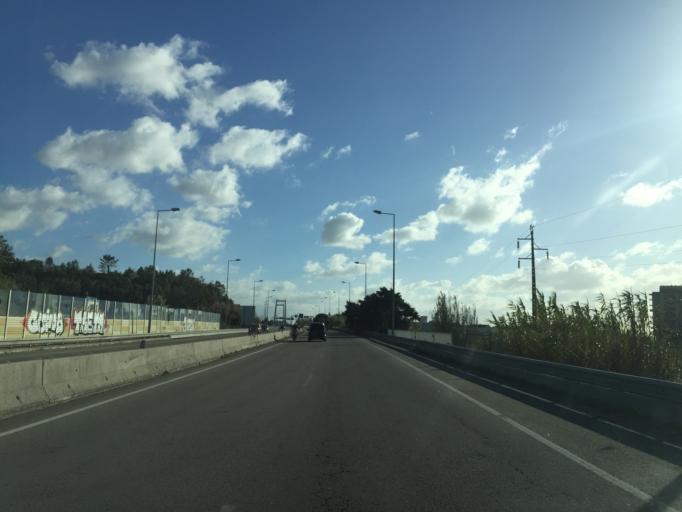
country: PT
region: Coimbra
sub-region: Figueira da Foz
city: Tavarede
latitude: 40.1574
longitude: -8.8412
